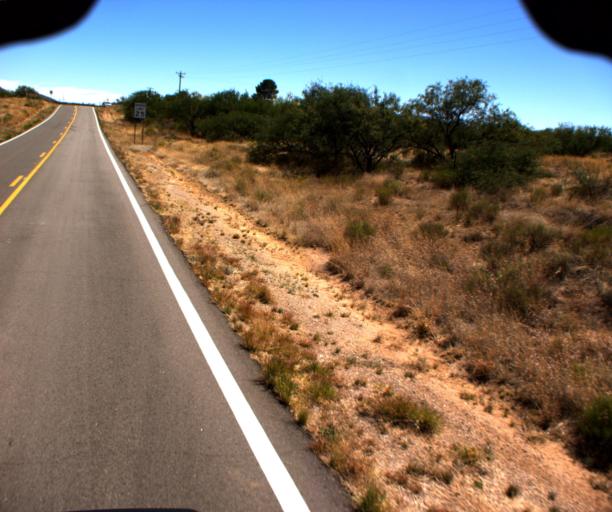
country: US
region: Arizona
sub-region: Santa Cruz County
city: Tubac
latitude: 31.4995
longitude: -111.5460
